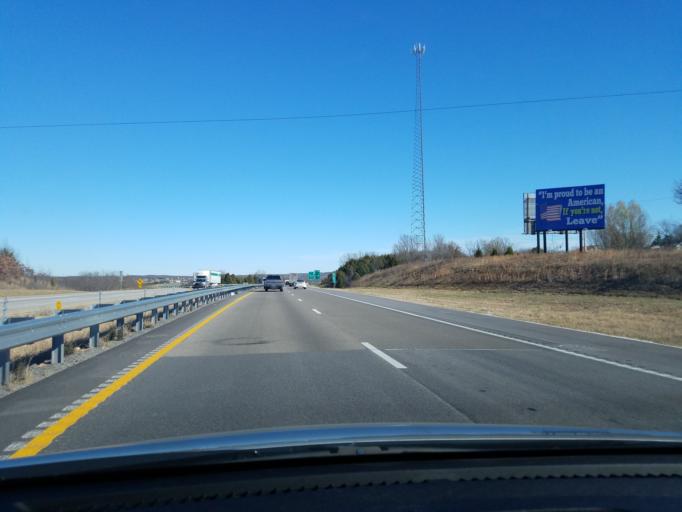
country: US
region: Missouri
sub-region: Greene County
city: Strafford
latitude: 37.2998
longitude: -93.0121
